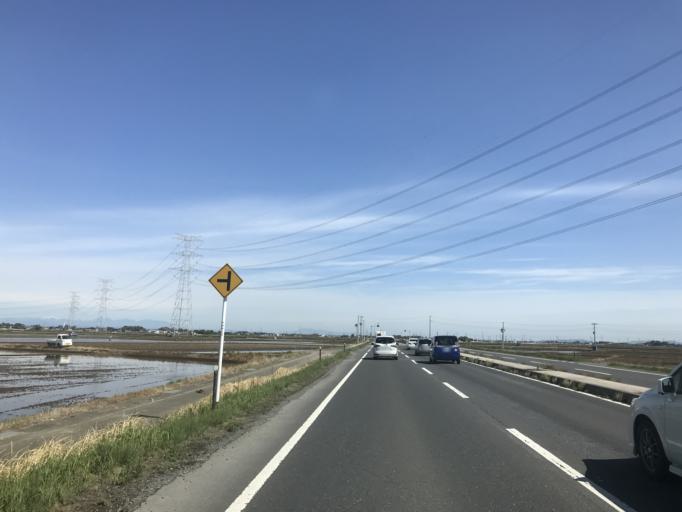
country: JP
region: Ibaraki
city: Ishige
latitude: 36.1234
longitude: 139.9823
